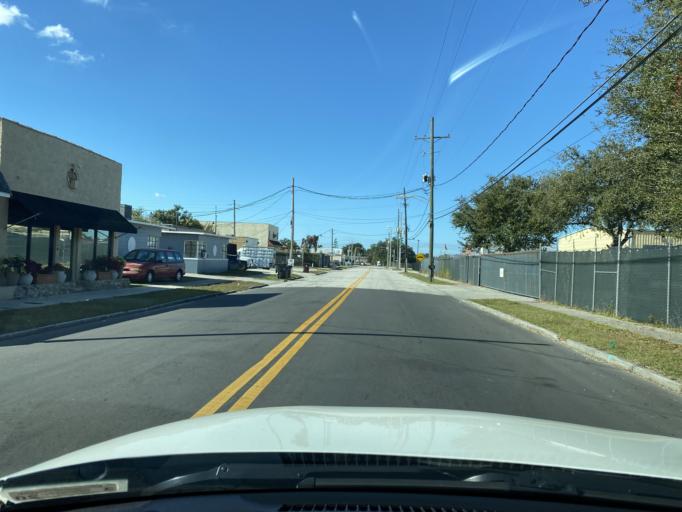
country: US
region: Florida
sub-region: Orange County
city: Orlando
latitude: 28.5457
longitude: -81.3944
